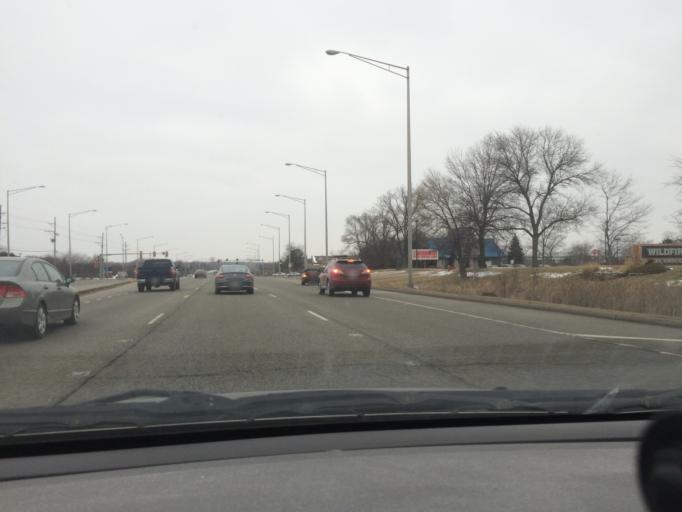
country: US
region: Illinois
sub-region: Cook County
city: Hoffman Estates
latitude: 42.0395
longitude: -88.0479
